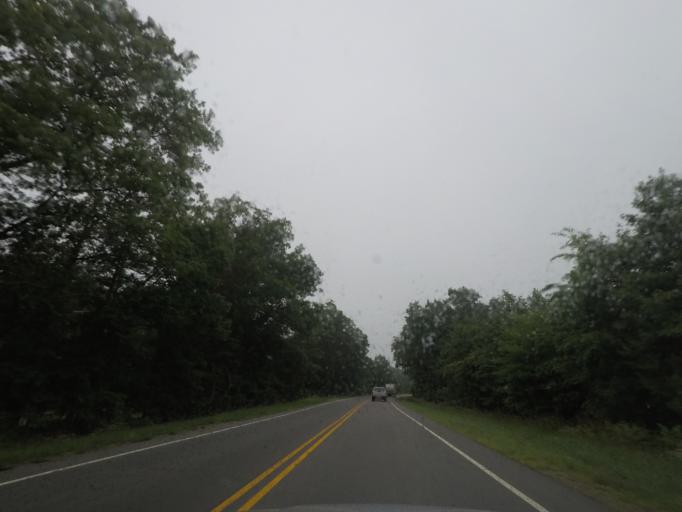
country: US
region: Virginia
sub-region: Buckingham County
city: Buckingham
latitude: 37.4985
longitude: -78.4771
